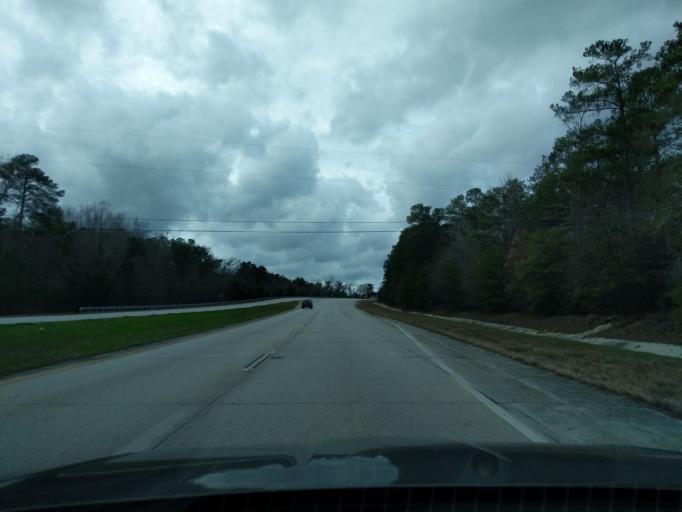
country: US
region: Georgia
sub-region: Columbia County
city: Evans
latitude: 33.4692
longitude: -82.1231
